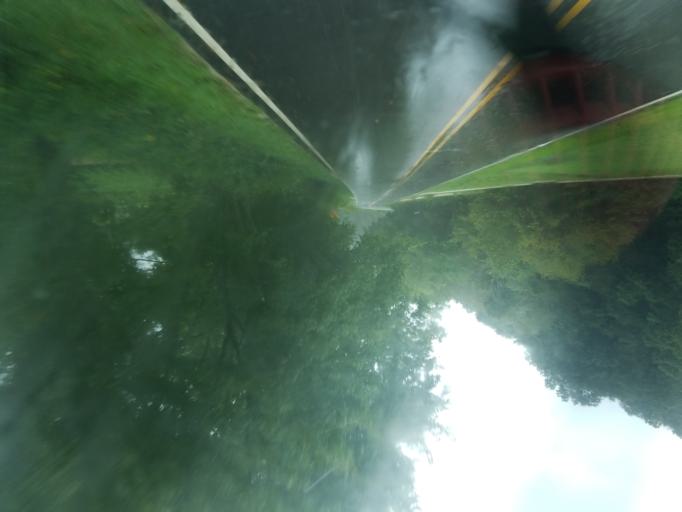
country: US
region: Kentucky
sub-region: Carter County
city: Grayson
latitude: 38.4950
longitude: -83.0107
